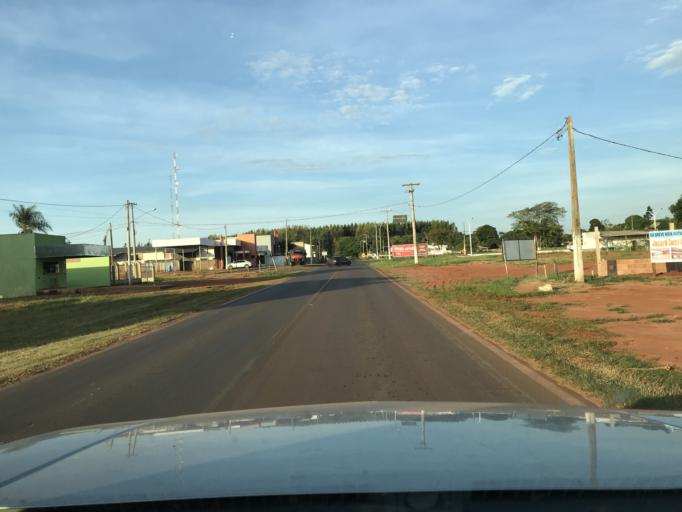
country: BR
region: Mato Grosso do Sul
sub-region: Iguatemi
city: Iguatemi
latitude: -23.6627
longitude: -54.5644
